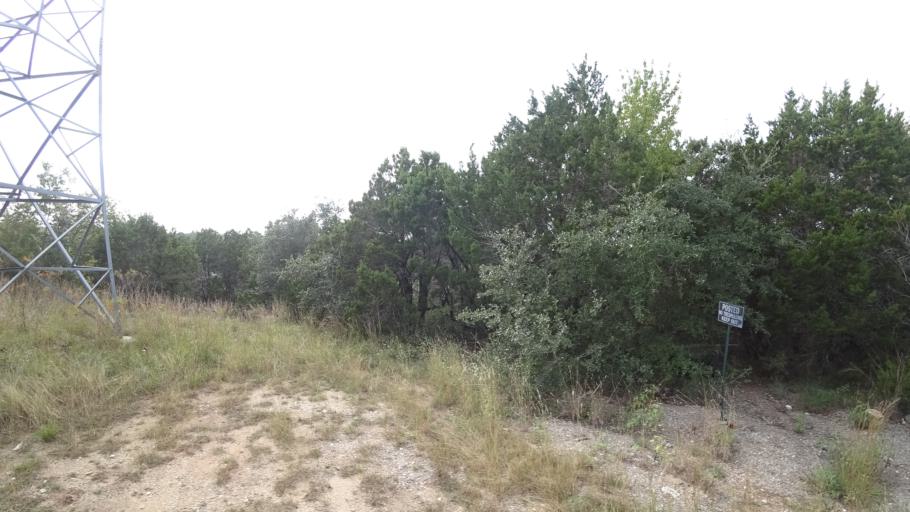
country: US
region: Texas
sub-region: Travis County
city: Hudson Bend
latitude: 30.3878
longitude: -97.9230
